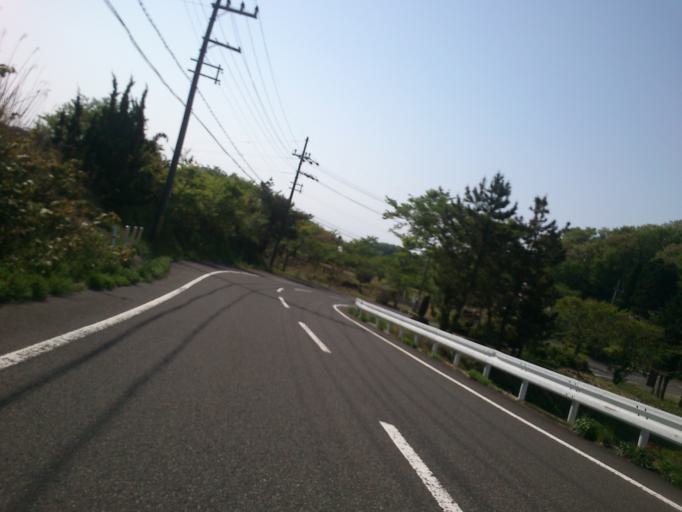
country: JP
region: Kyoto
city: Miyazu
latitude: 35.7189
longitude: 135.1872
